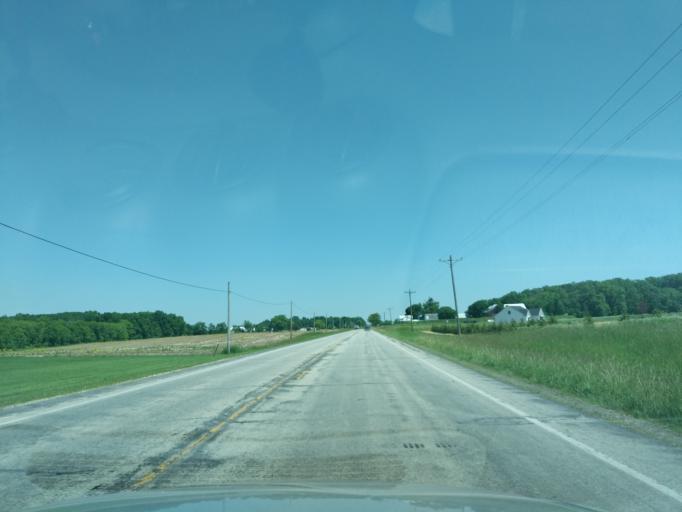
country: US
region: Indiana
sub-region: Whitley County
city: Columbia City
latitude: 41.0909
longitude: -85.4713
